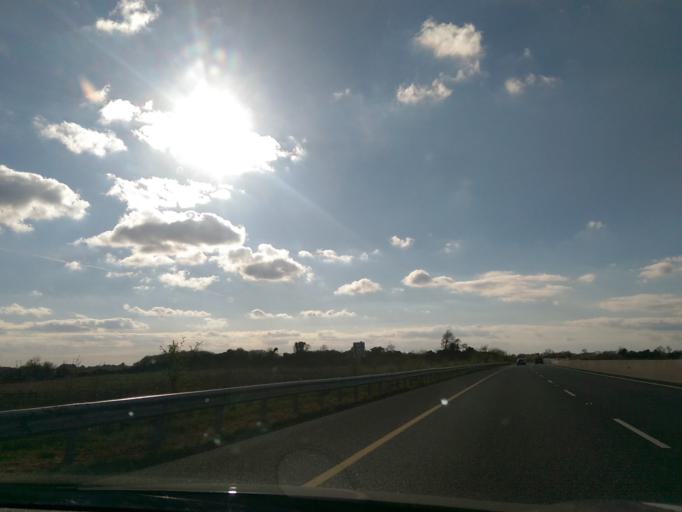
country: IE
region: Connaught
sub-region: County Galway
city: Loughrea
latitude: 53.2664
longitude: -8.6351
